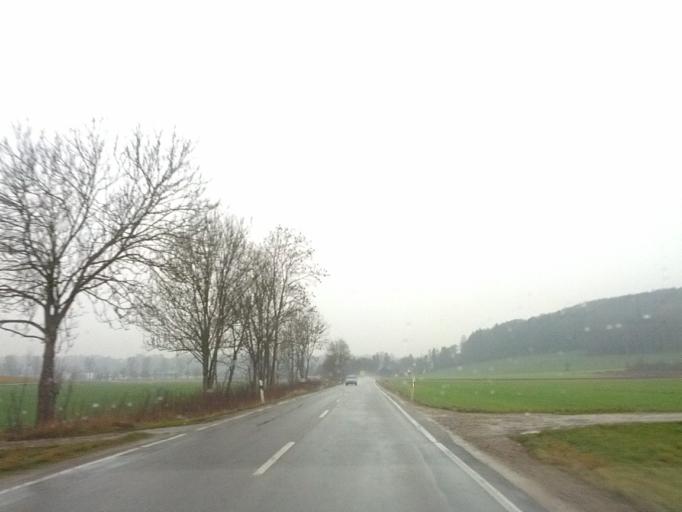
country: DE
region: Baden-Wuerttemberg
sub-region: Tuebingen Region
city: Ummendorf
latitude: 48.0739
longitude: 9.8348
